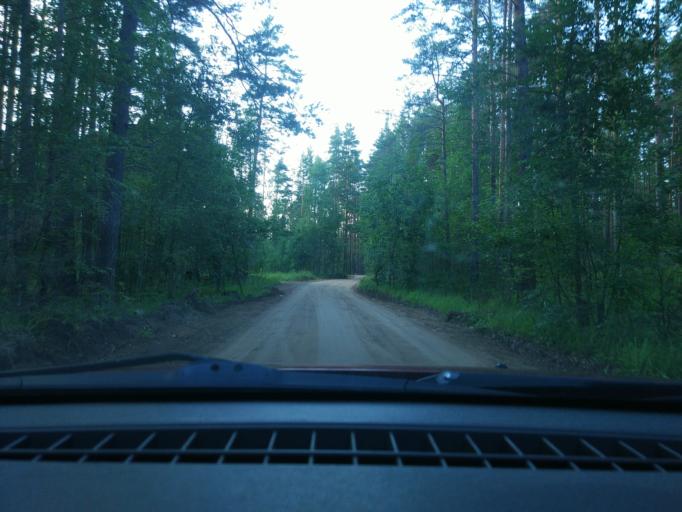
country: RU
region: Leningrad
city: Priozersk
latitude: 60.9289
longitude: 30.0545
